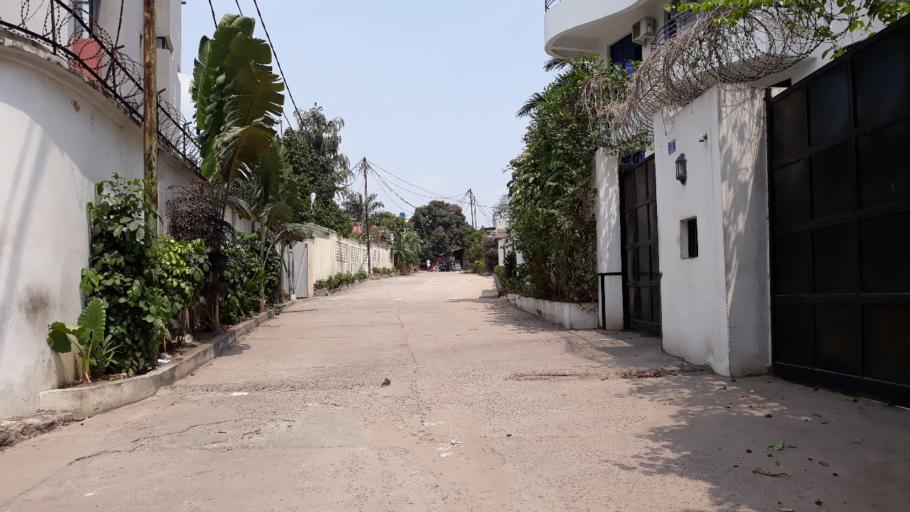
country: CD
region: Kinshasa
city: Kinshasa
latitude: -4.3263
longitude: 15.2769
